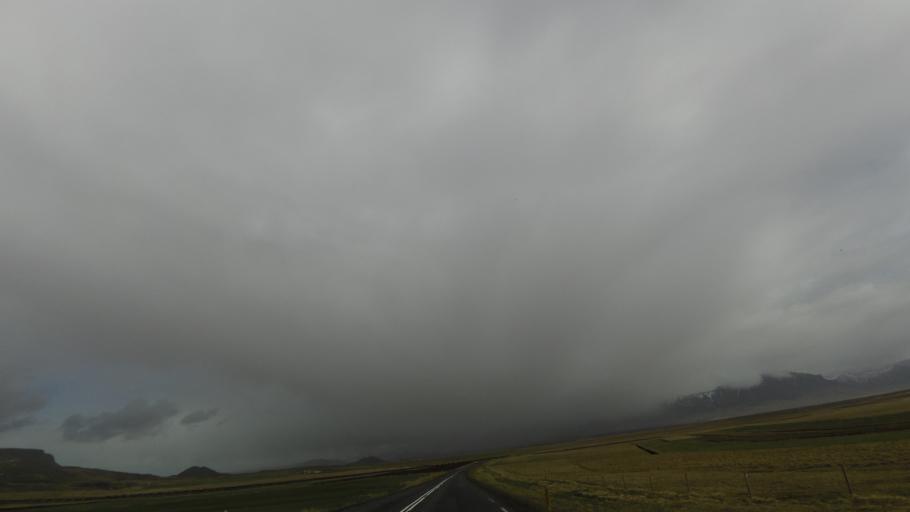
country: IS
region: West
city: Stykkisholmur
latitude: 64.8456
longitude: -22.4194
